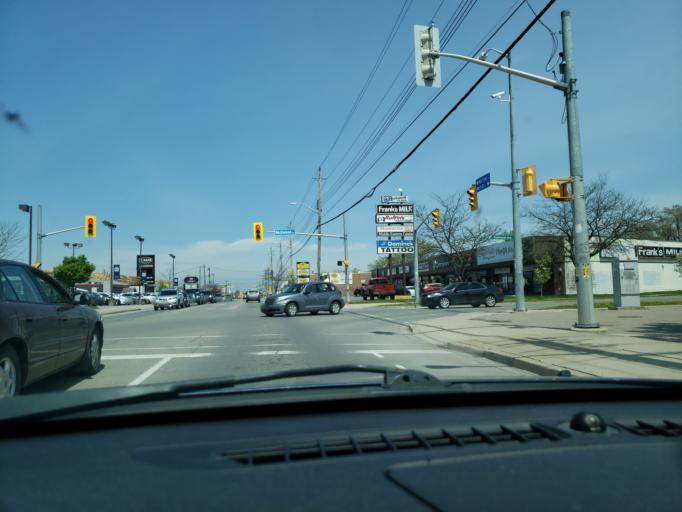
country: CA
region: Ontario
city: Thorold
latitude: 43.1463
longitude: -79.2141
